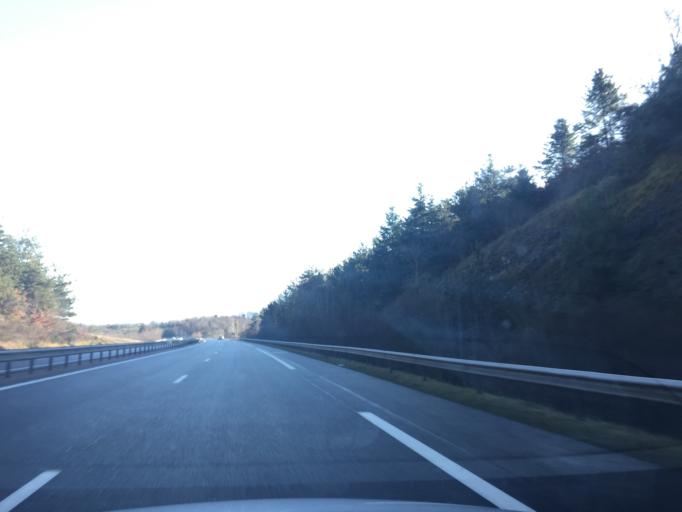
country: FR
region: Rhone-Alpes
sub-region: Departement de la Loire
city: Saint-Germain-Laval
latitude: 45.8622
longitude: 3.9664
